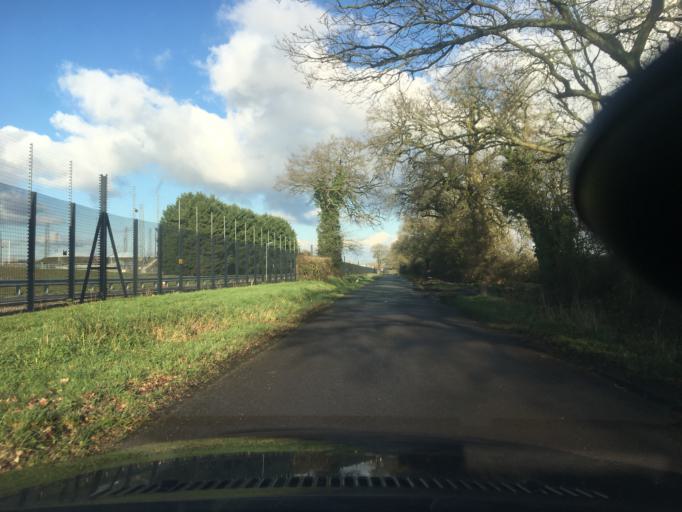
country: GB
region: England
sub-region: West Berkshire
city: Stratfield Mortimer
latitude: 51.4045
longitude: -1.0199
